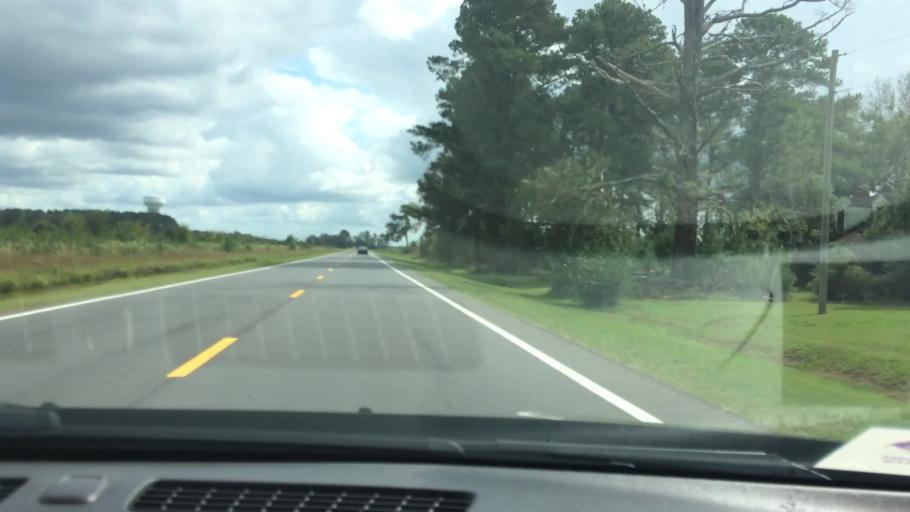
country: US
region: North Carolina
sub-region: Pitt County
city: Farmville
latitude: 35.5545
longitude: -77.5532
